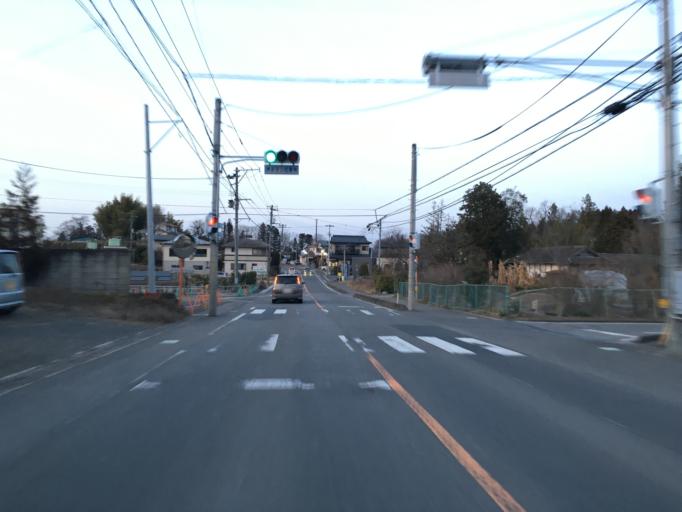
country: JP
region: Fukushima
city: Ishikawa
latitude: 37.1145
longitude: 140.3506
